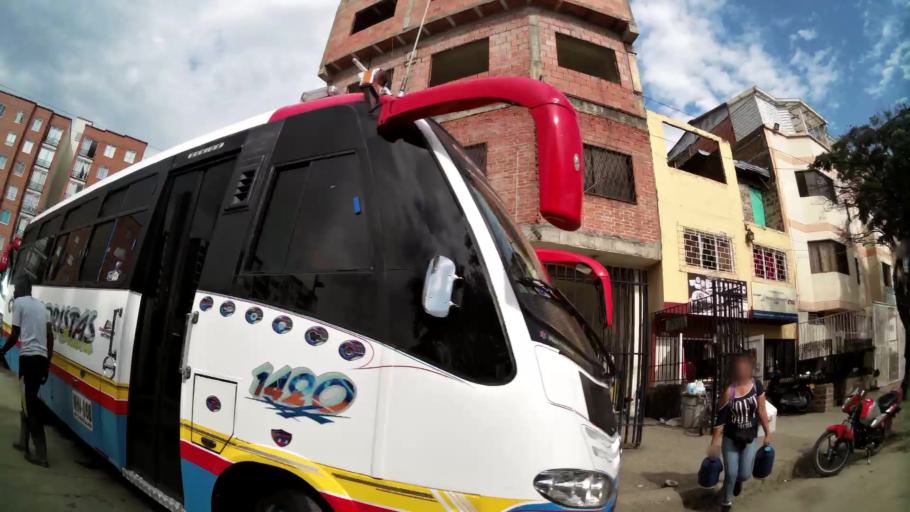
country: CO
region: Valle del Cauca
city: Cali
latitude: 3.4672
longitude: -76.5211
